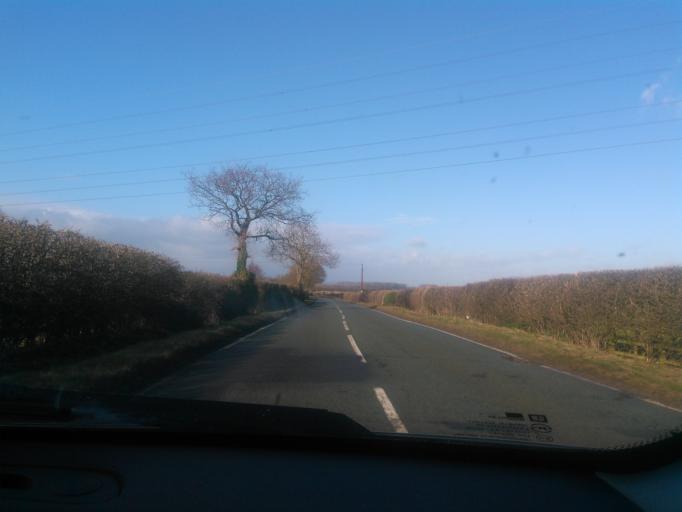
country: GB
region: England
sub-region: Telford and Wrekin
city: Eyton upon the Weald Moors
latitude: 52.7245
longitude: -2.5452
